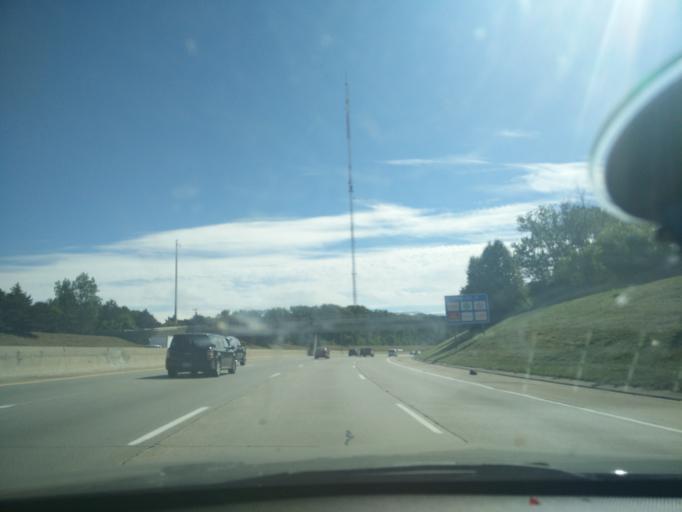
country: US
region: Michigan
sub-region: Oakland County
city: Lathrup Village
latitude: 42.4866
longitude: -83.2104
